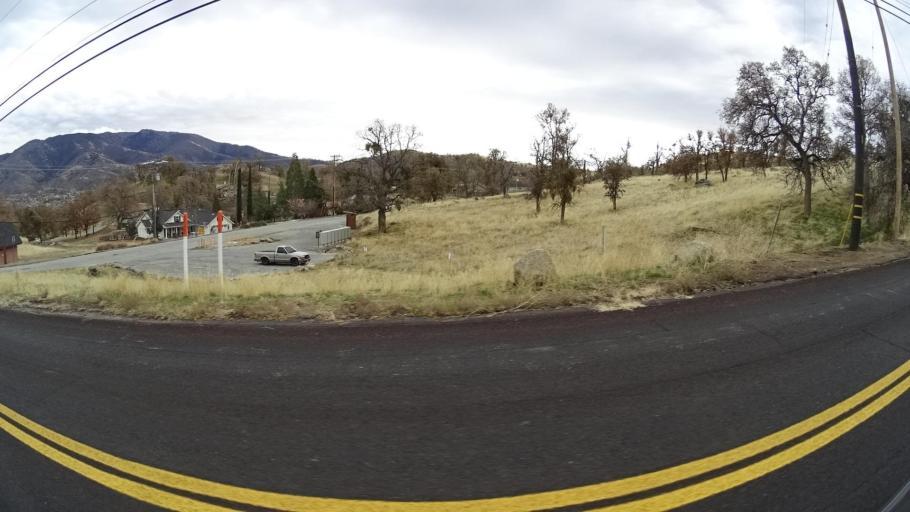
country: US
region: California
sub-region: Kern County
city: Stallion Springs
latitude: 35.0922
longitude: -118.6517
